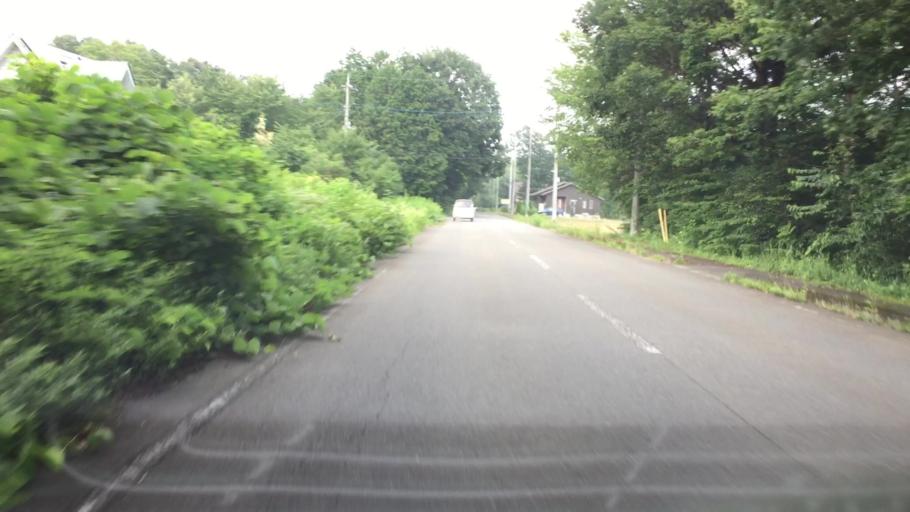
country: JP
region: Tochigi
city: Kuroiso
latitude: 36.9331
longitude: 139.9571
